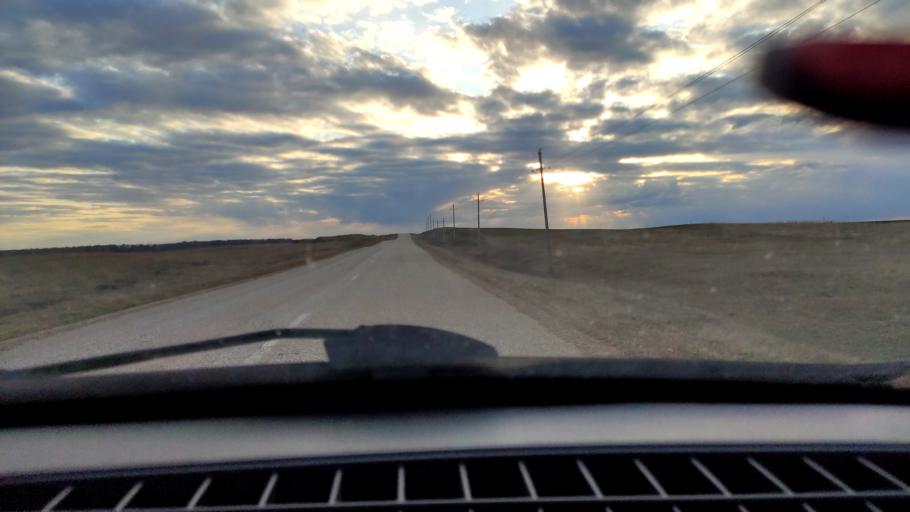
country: RU
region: Bashkortostan
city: Tolbazy
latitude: 54.0043
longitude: 55.6426
